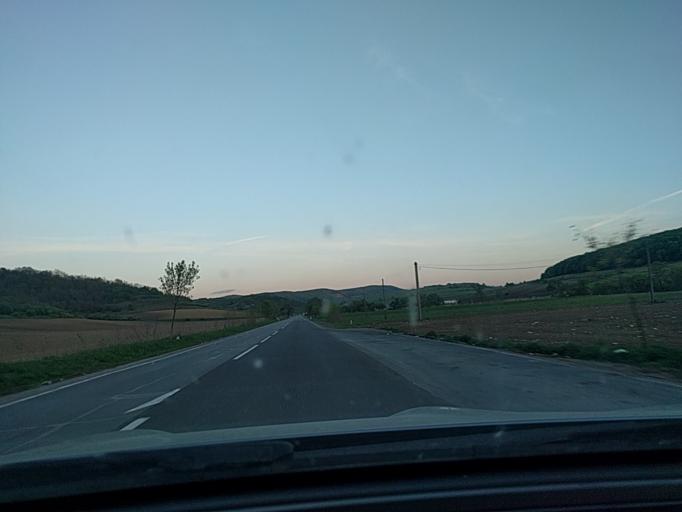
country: RO
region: Mures
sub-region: Comuna Nades
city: Nades
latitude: 46.3253
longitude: 24.7145
